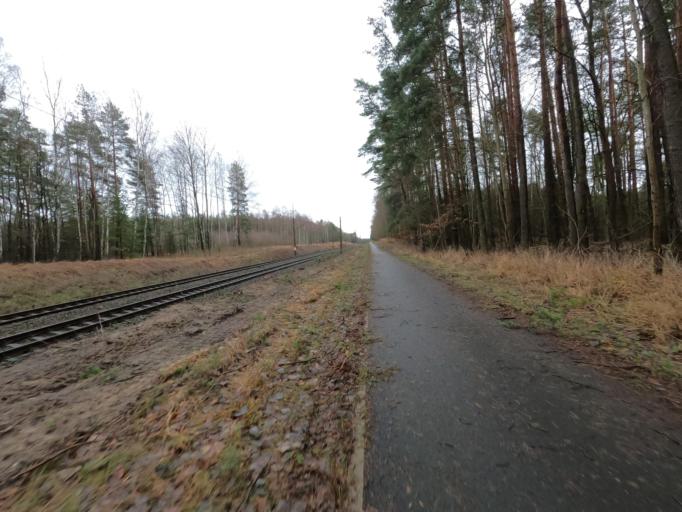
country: PL
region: Greater Poland Voivodeship
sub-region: Powiat pilski
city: Kaczory
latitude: 53.1193
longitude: 16.8273
